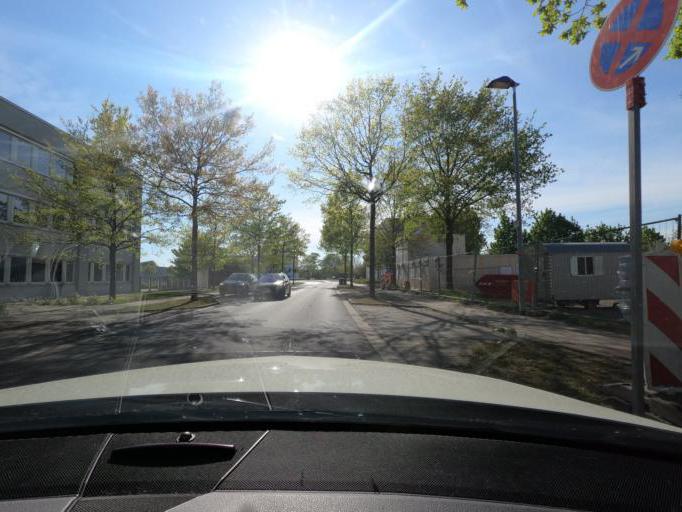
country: DE
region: North Rhine-Westphalia
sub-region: Regierungsbezirk Dusseldorf
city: Moers
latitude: 51.4729
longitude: 6.5963
